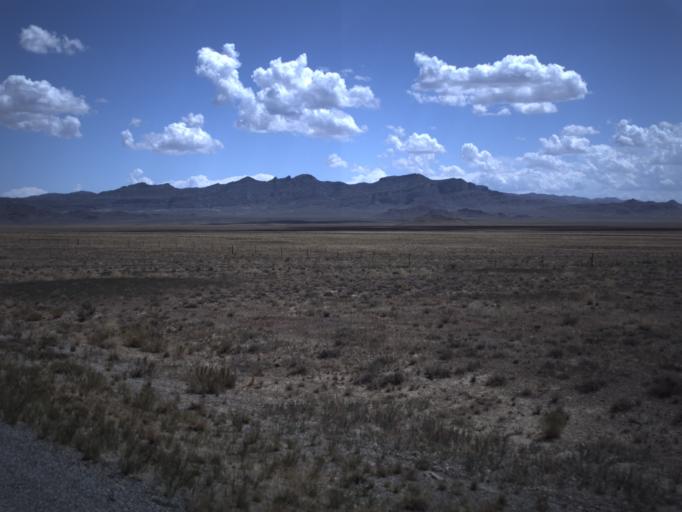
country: US
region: Utah
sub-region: Beaver County
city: Milford
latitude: 39.0426
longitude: -113.8063
